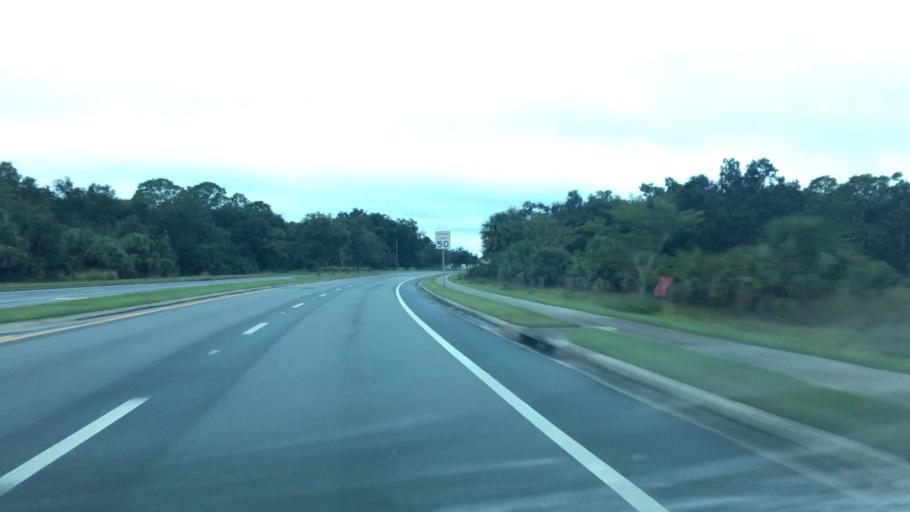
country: US
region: Florida
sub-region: Seminole County
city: Midway
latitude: 28.7578
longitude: -81.2312
